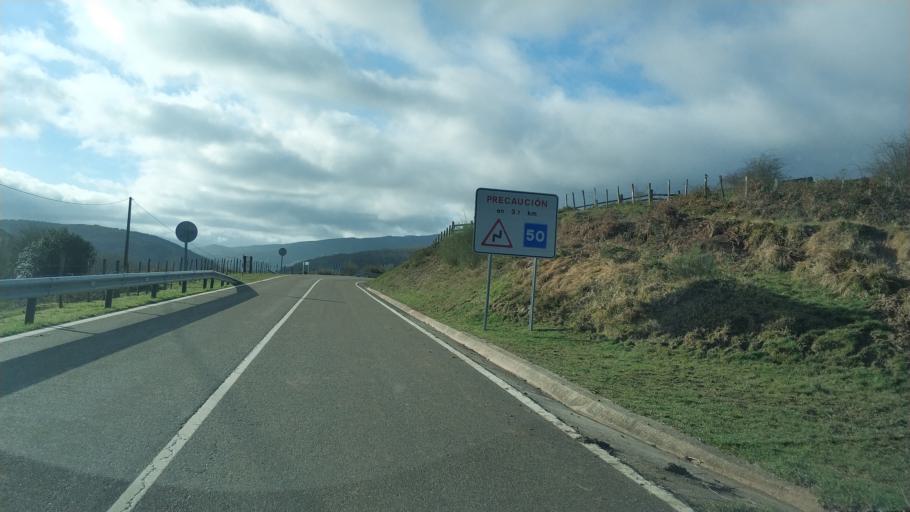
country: ES
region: Cantabria
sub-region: Provincia de Cantabria
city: Reinosa
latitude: 42.9670
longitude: -4.0609
